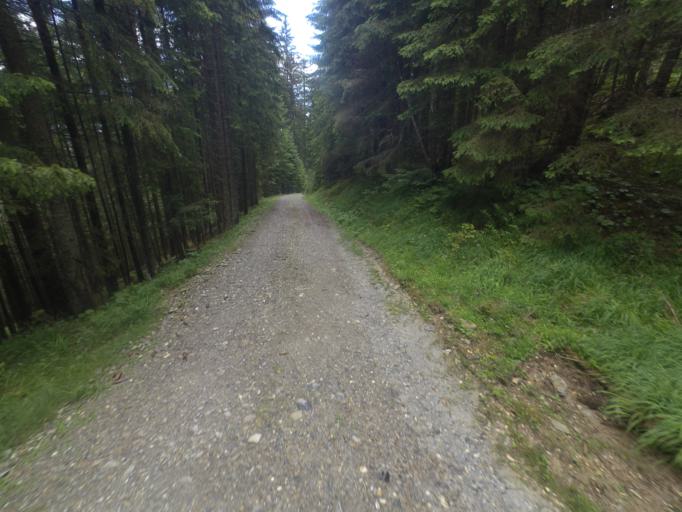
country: AT
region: Salzburg
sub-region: Politischer Bezirk Sankt Johann im Pongau
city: Schwarzach im Pongau
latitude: 47.3049
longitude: 13.1585
